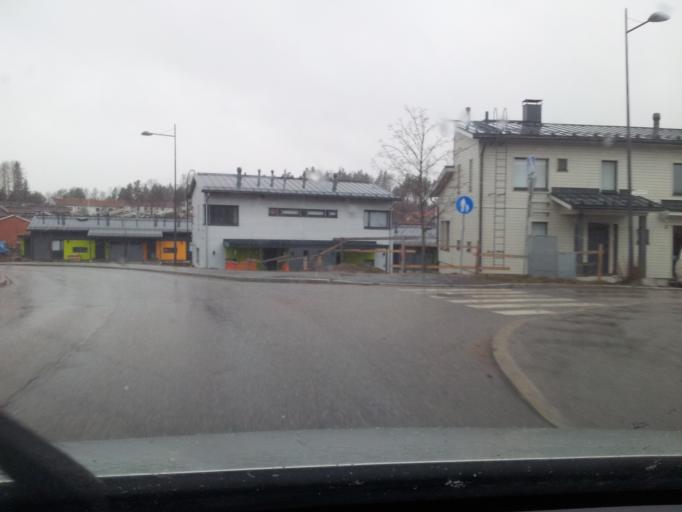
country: FI
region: Uusimaa
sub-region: Helsinki
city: Espoo
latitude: 60.1945
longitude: 24.5956
